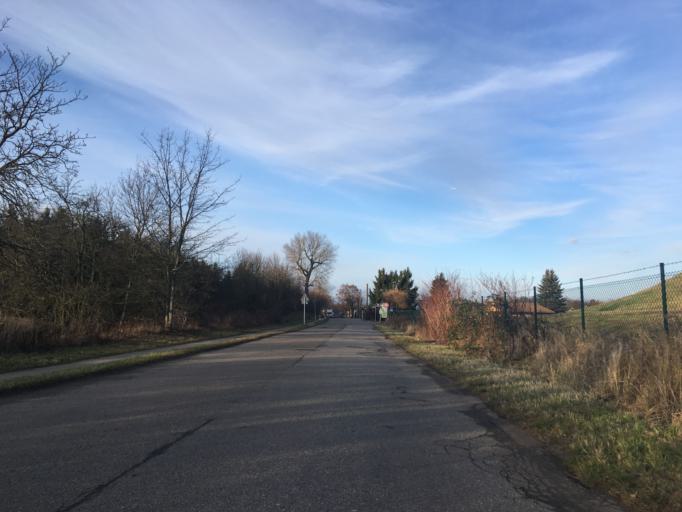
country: DE
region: Berlin
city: Blankenfelde
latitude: 52.6383
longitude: 13.4009
